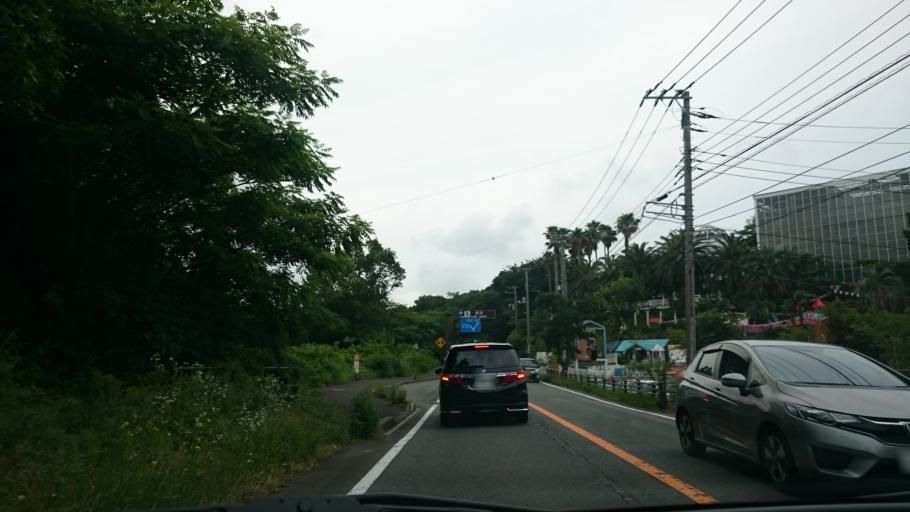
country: JP
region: Shizuoka
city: Ito
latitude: 34.9211
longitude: 139.1194
